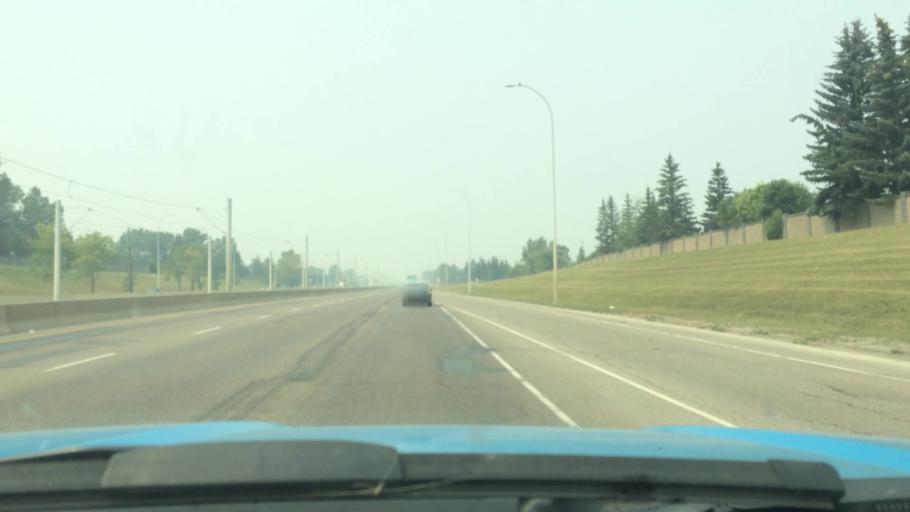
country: CA
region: Alberta
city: Calgary
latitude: 51.1128
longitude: -114.1830
